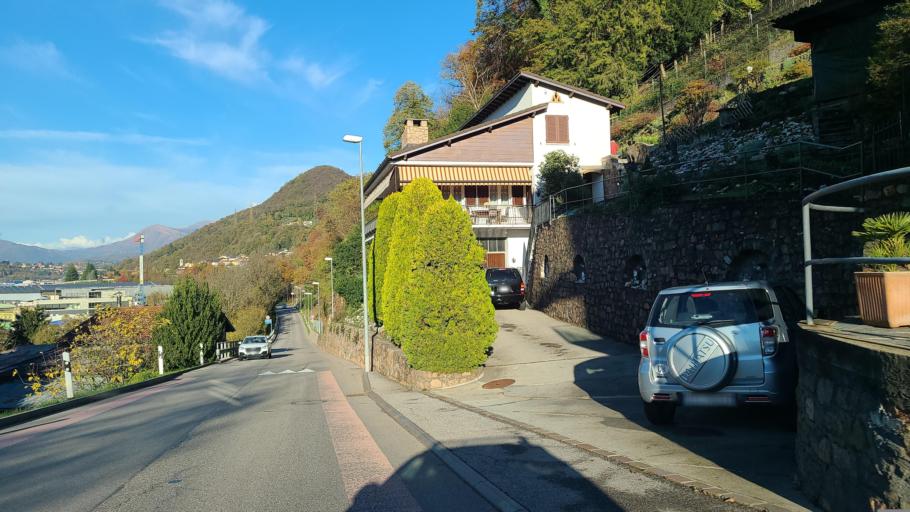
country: CH
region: Ticino
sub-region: Lugano District
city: Montagnola
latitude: 45.9594
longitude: 8.9232
